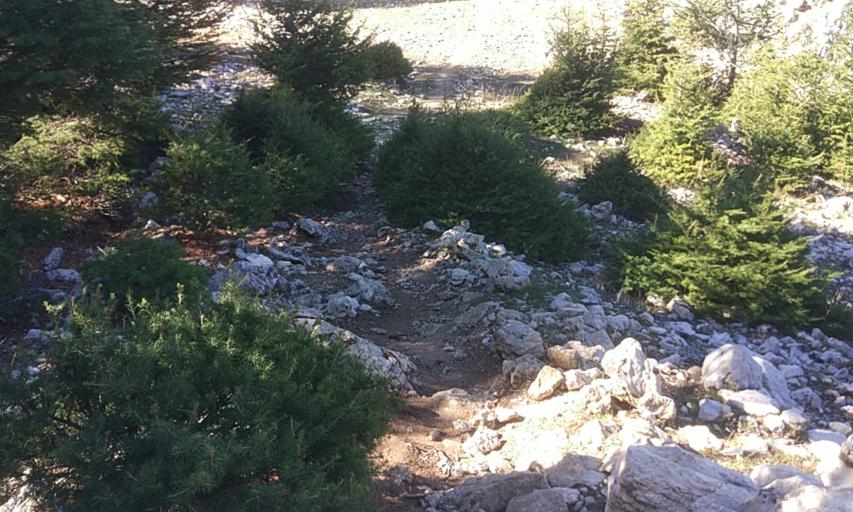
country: TR
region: Antalya
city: Altinyaka
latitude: 36.5495
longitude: 30.4136
